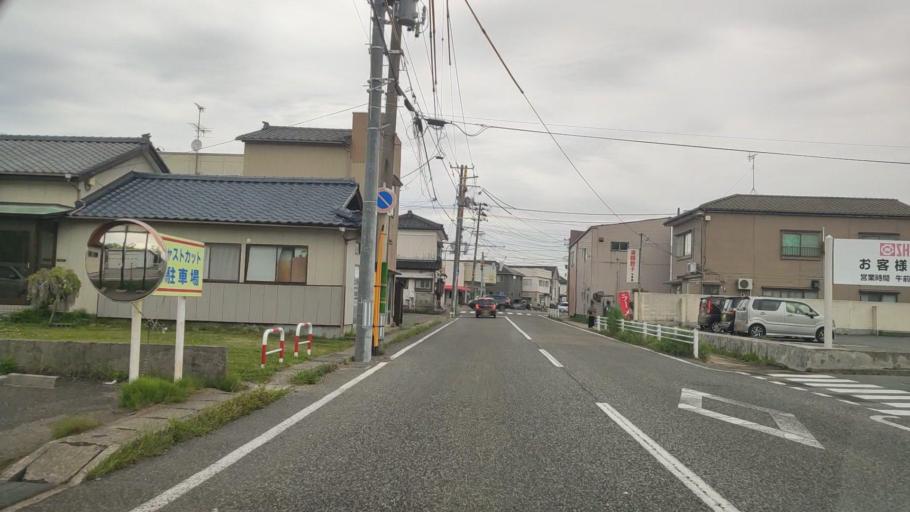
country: JP
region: Niigata
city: Niigata-shi
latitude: 37.9382
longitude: 139.0736
